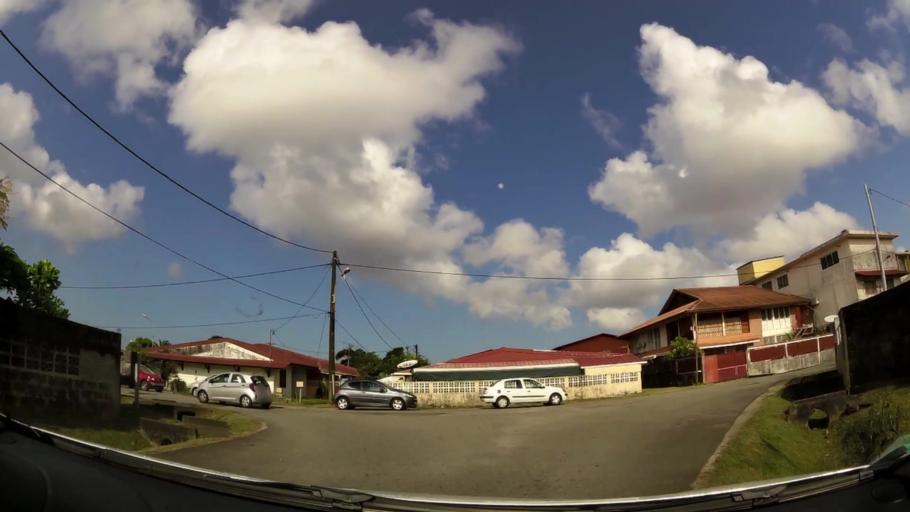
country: GF
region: Guyane
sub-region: Guyane
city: Cayenne
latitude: 4.9334
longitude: -52.3230
